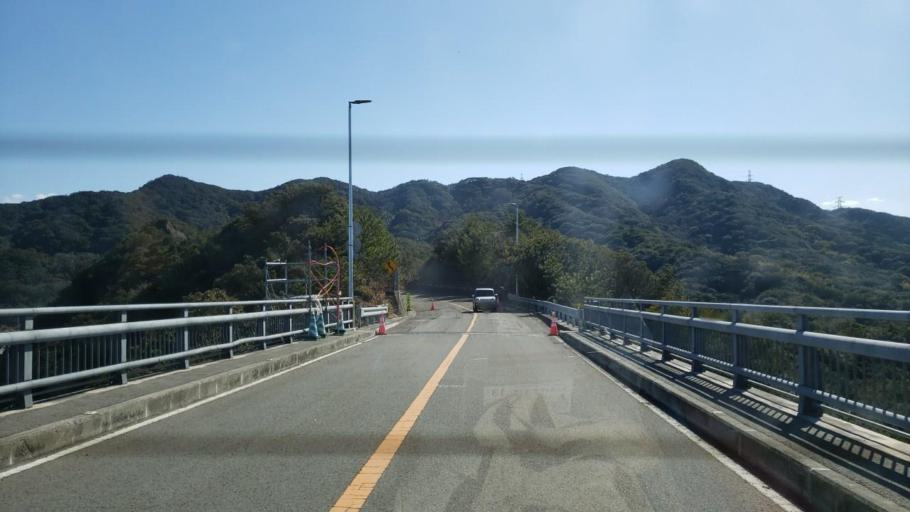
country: JP
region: Tokushima
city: Narutocho-mitsuishi
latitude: 34.2319
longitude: 134.6169
